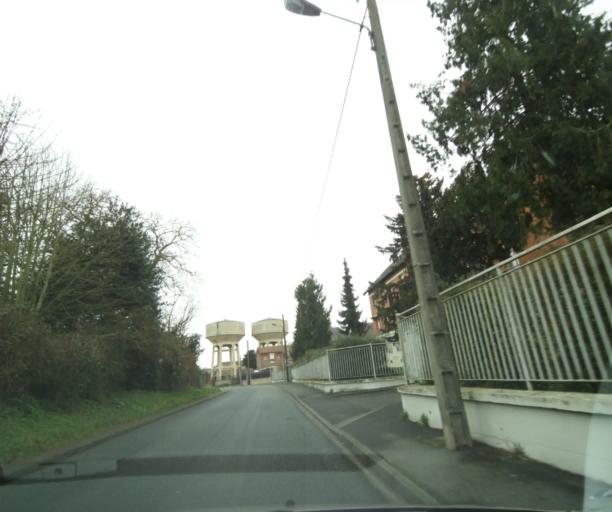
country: FR
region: Picardie
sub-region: Departement de l'Oise
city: Noyon
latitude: 49.5860
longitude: 3.0028
